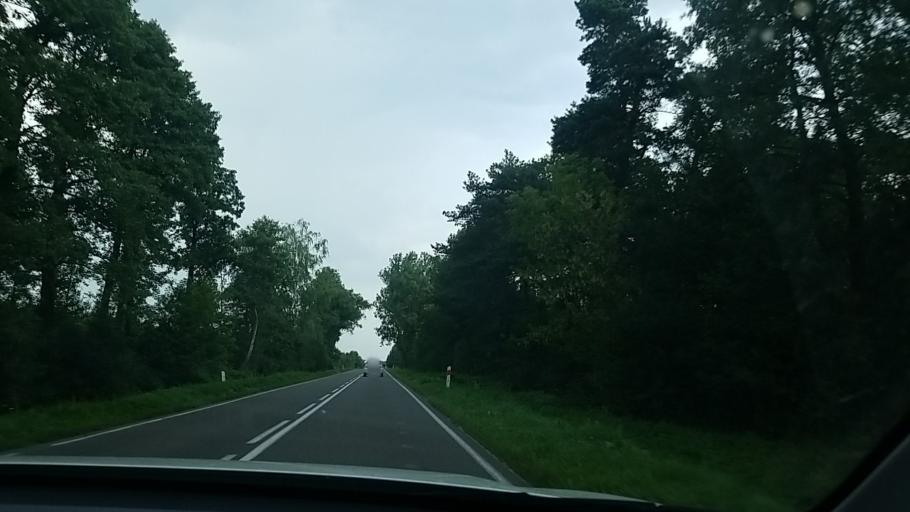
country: PL
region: Lublin Voivodeship
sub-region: Powiat leczynski
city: Cycow
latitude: 51.2483
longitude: 23.0911
